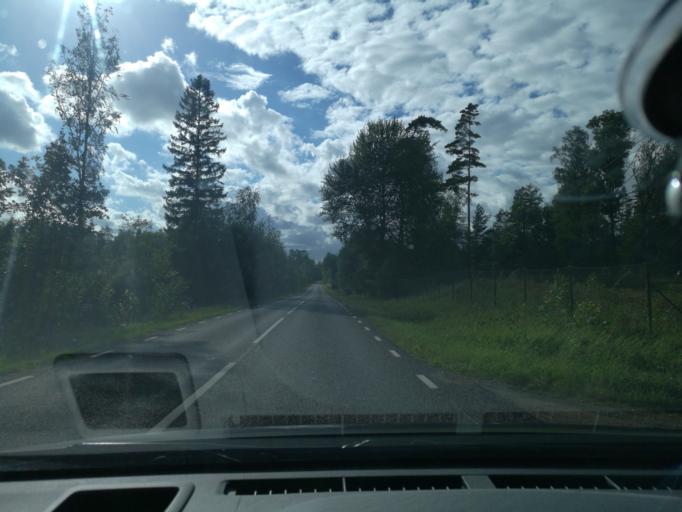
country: SE
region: Kronoberg
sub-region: Vaxjo Kommun
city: Braas
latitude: 57.0638
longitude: 15.0250
